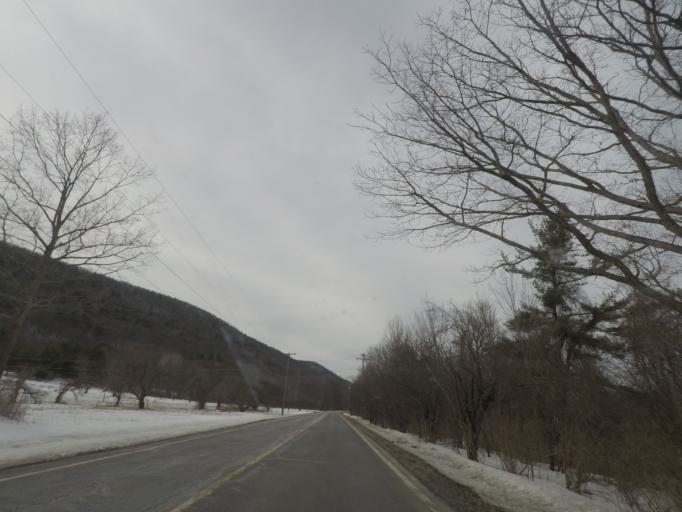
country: US
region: New York
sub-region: Albany County
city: Altamont
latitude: 42.6729
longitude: -74.0116
